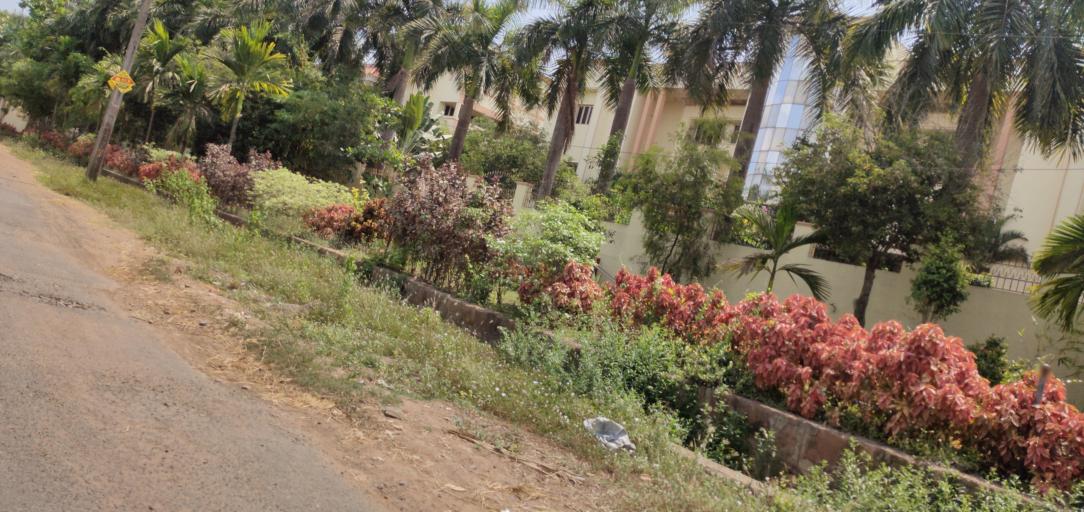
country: IN
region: Andhra Pradesh
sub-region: West Godavari
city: Tadepallegudem
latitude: 16.8579
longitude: 81.4940
